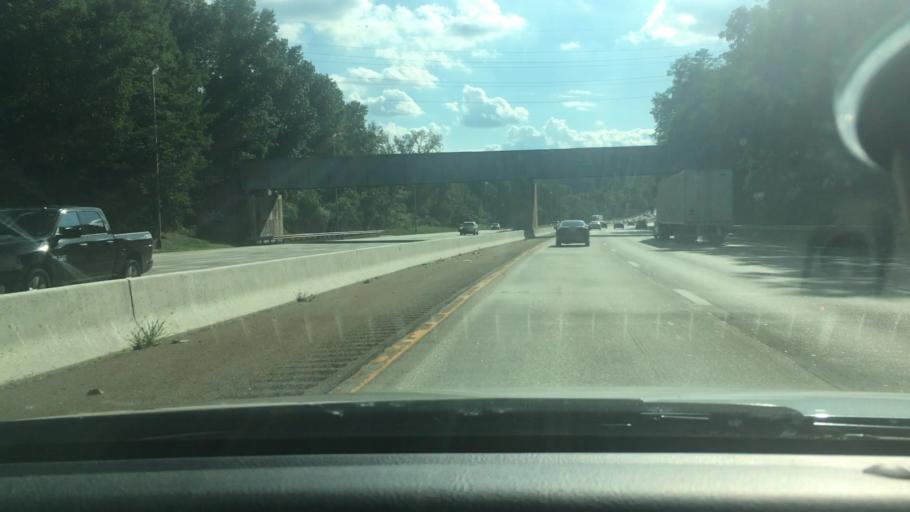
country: US
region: New Jersey
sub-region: Morris County
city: Boonton
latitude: 40.9188
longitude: -74.3659
